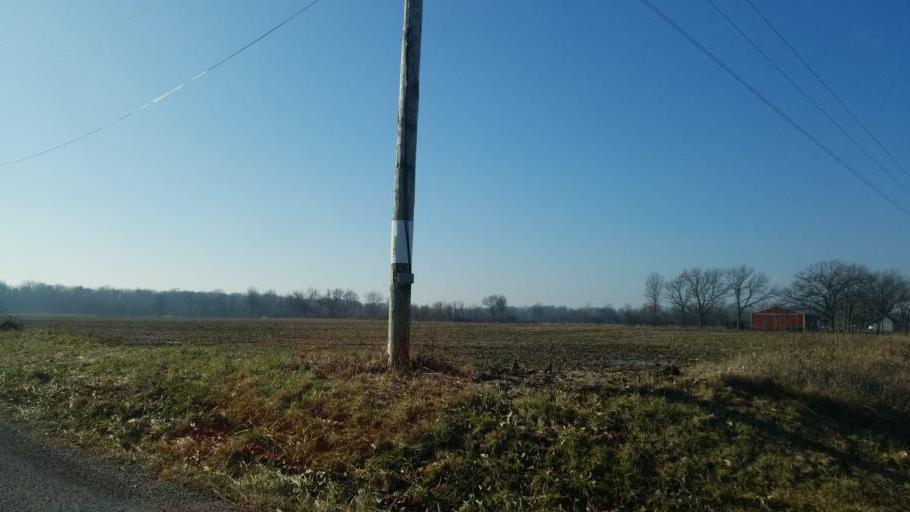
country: US
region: Ohio
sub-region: Seneca County
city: Tiffin
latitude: 41.1244
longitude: -83.1121
